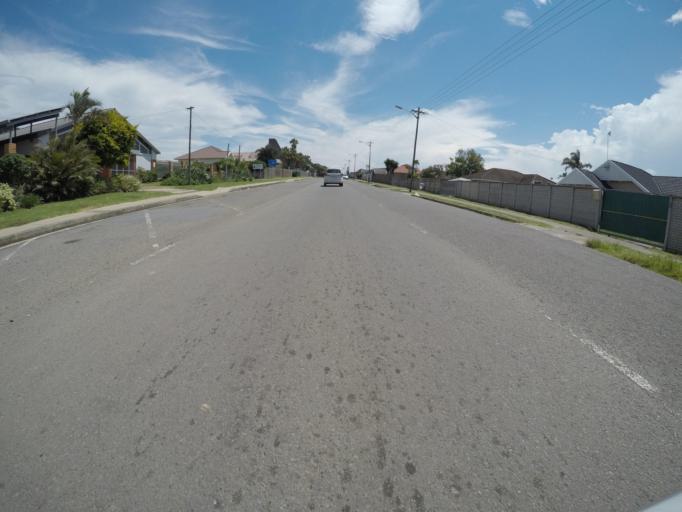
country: ZA
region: Eastern Cape
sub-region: Buffalo City Metropolitan Municipality
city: East London
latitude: -33.0350
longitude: 27.8621
